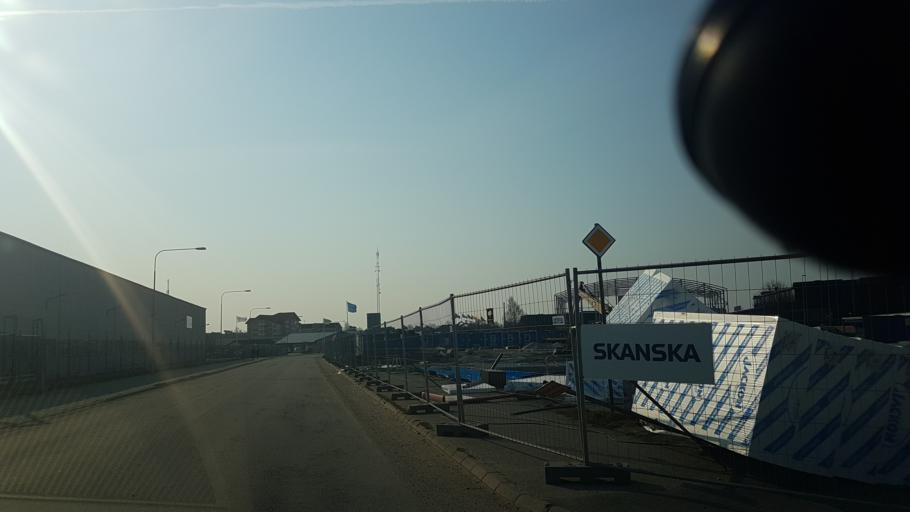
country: SE
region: Skane
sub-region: Ystads Kommun
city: Ystad
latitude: 55.4355
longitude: 13.8333
